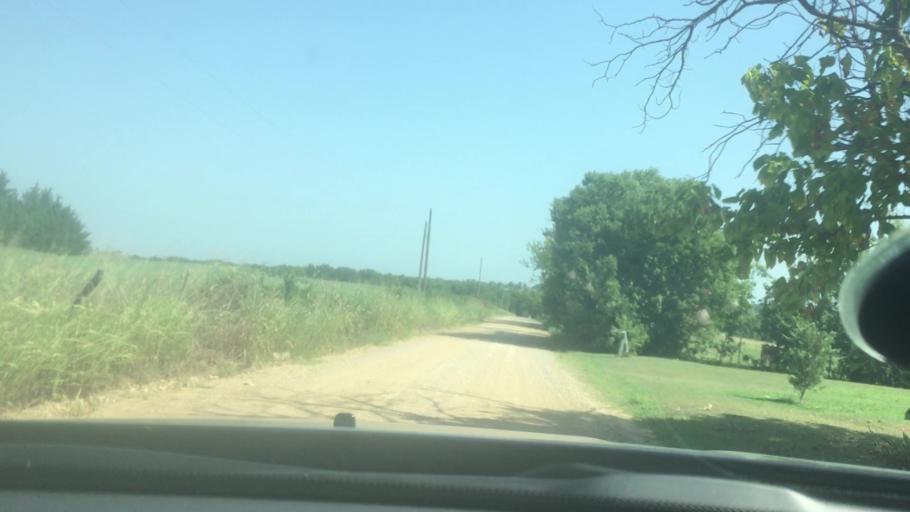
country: US
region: Oklahoma
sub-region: Bryan County
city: Durant
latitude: 34.0940
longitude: -96.4077
